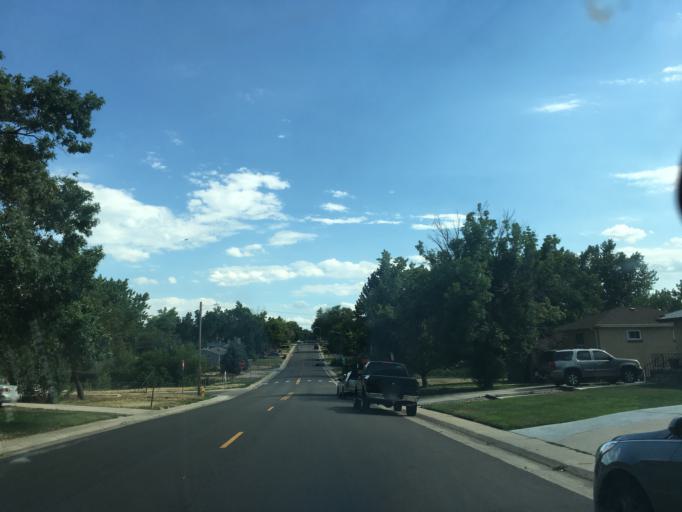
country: US
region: Colorado
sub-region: Jefferson County
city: Lakewood
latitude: 39.6861
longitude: -105.0443
